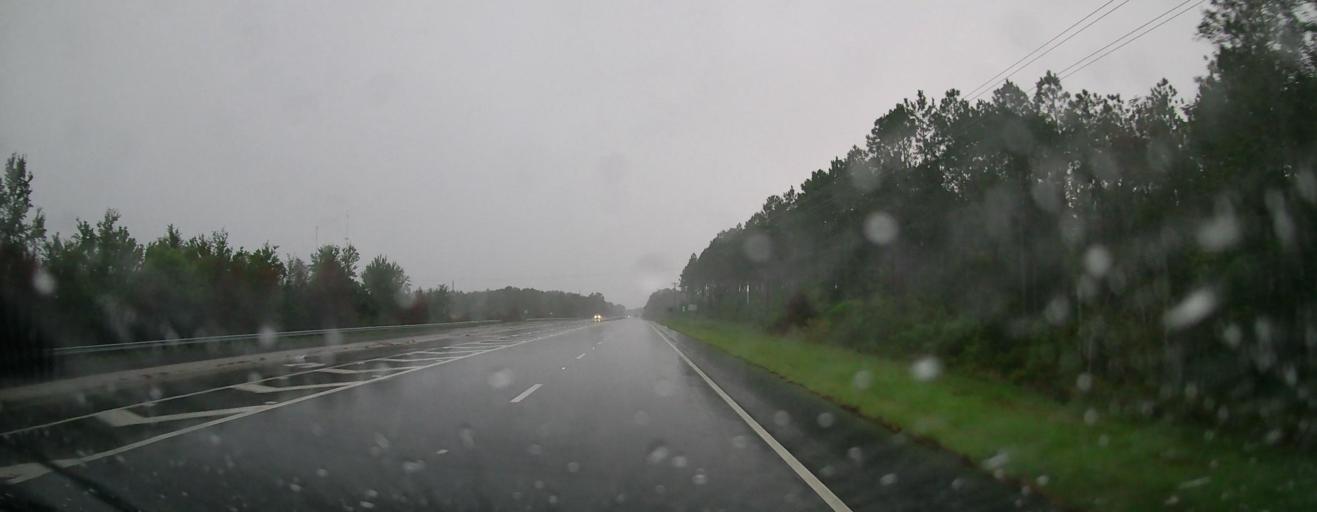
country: US
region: Georgia
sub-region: Clinch County
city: Homerville
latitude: 31.0483
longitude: -82.7160
